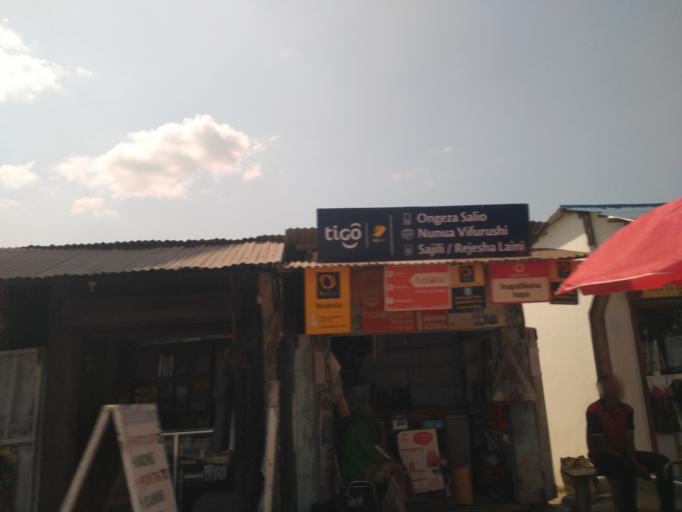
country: TZ
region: Dar es Salaam
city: Dar es Salaam
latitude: -6.8219
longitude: 39.3034
